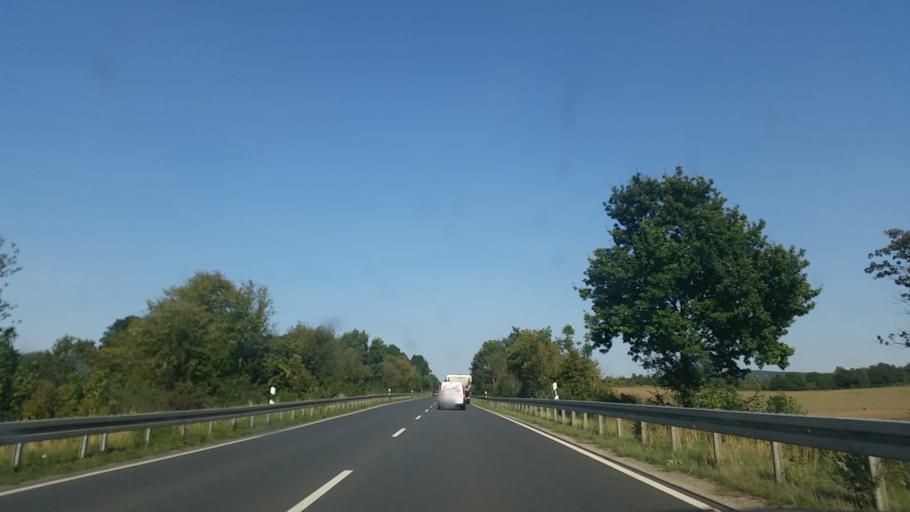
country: DE
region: Lower Saxony
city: Coppenbrugge
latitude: 52.1169
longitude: 9.5189
